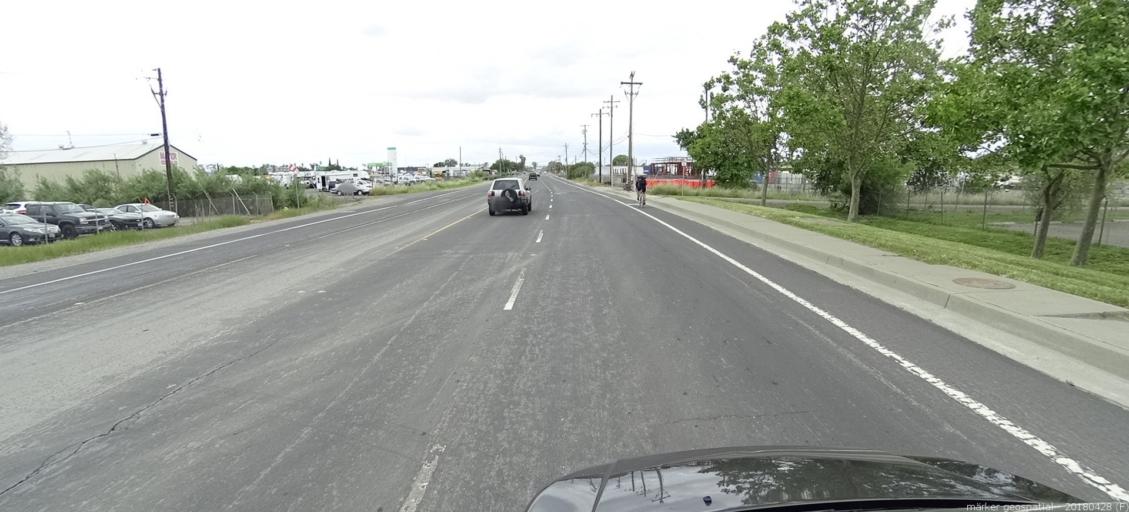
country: US
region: California
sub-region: Yolo County
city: West Sacramento
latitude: 38.5779
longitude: -121.5684
